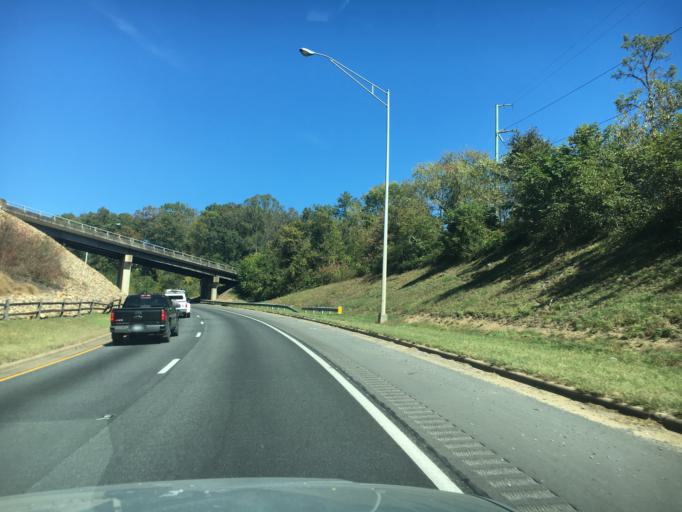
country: US
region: North Carolina
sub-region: Buncombe County
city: Asheville
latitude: 35.5669
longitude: -82.5868
